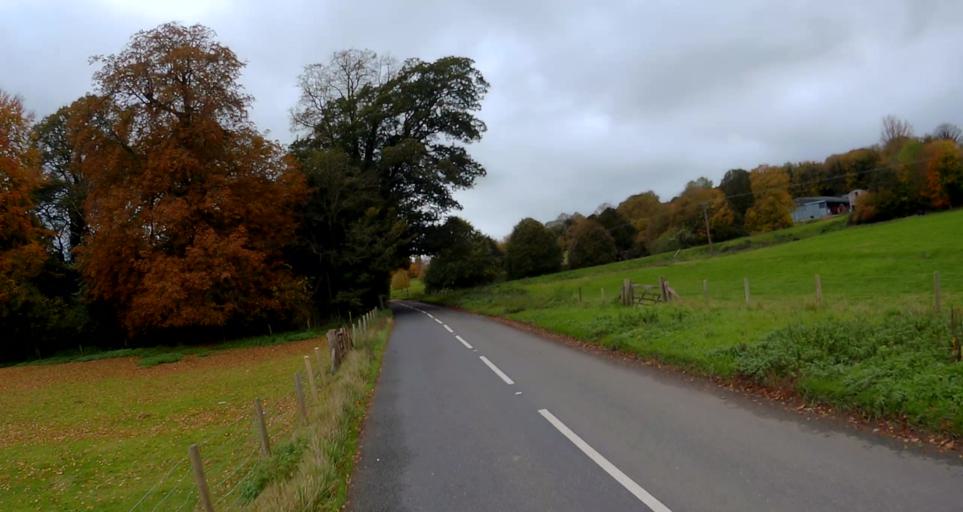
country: GB
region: England
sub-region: Hampshire
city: Four Marks
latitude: 51.1582
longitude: -1.1522
